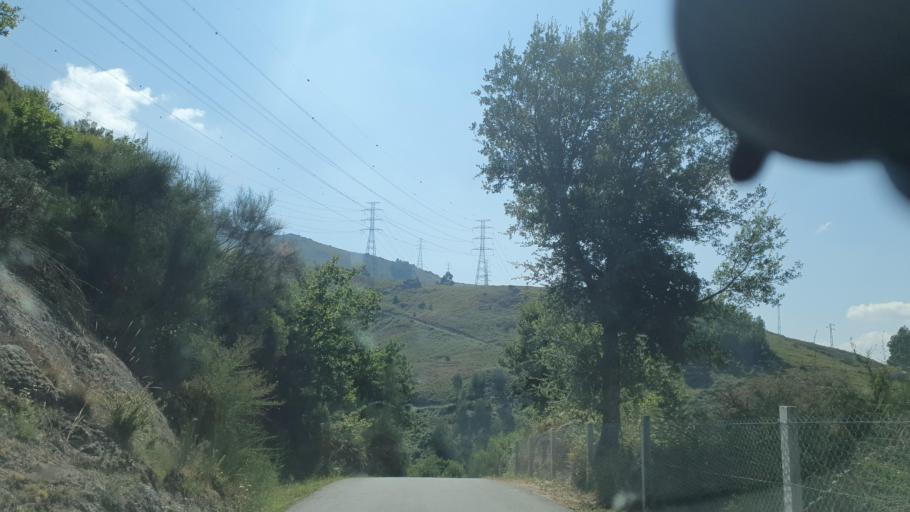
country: PT
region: Braga
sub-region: Vieira do Minho
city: Vieira do Minho
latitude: 41.6732
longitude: -8.1312
